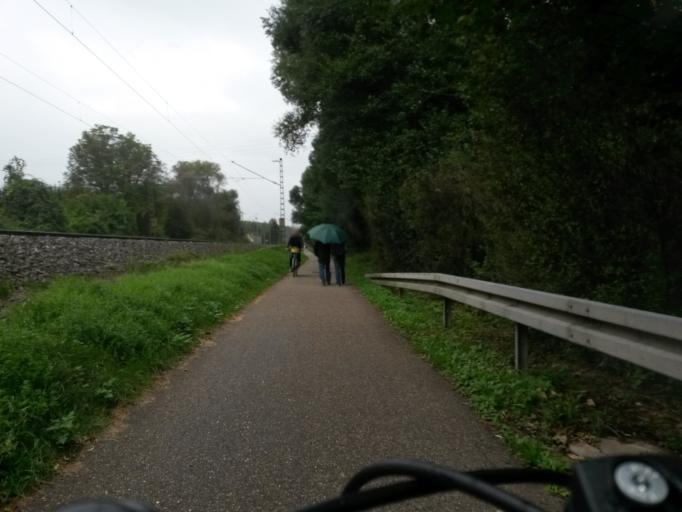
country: DE
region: Baden-Wuerttemberg
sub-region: Karlsruhe Region
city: Konigsbach-Stein
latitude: 48.9608
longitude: 8.5594
